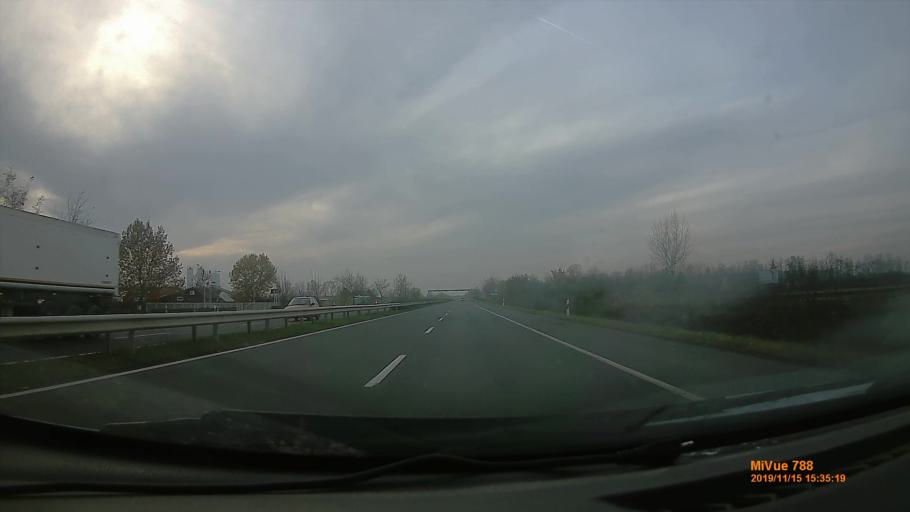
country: HU
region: Bekes
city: Gyula
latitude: 46.6544
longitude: 21.2305
